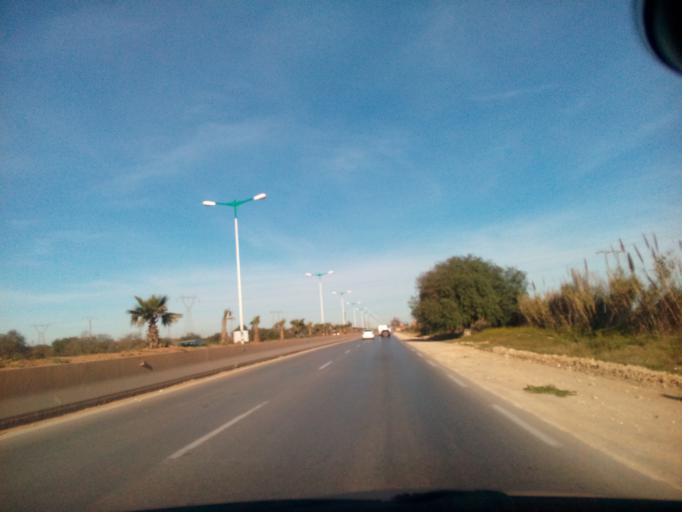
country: DZ
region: Mostaganem
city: Mostaganem
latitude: 35.8721
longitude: 0.1480
